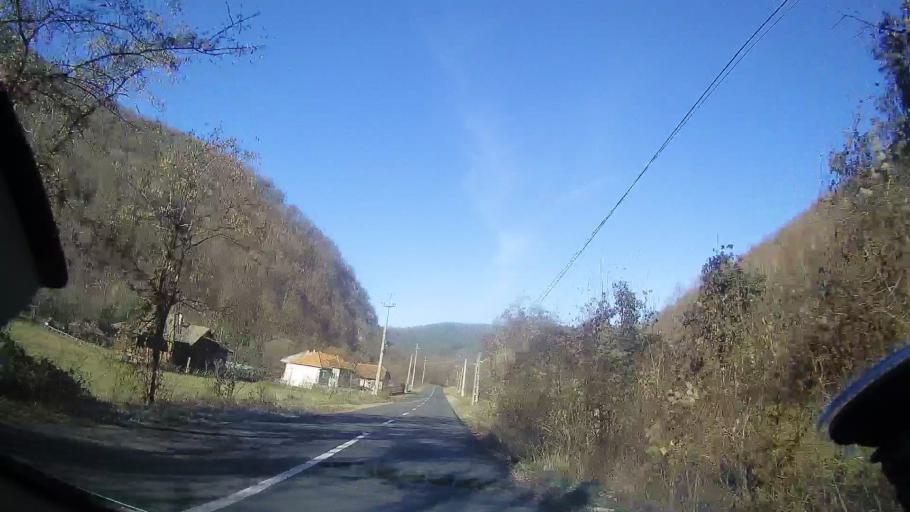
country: RO
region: Bihor
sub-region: Comuna Bulz
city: Bulz
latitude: 46.9175
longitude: 22.6556
